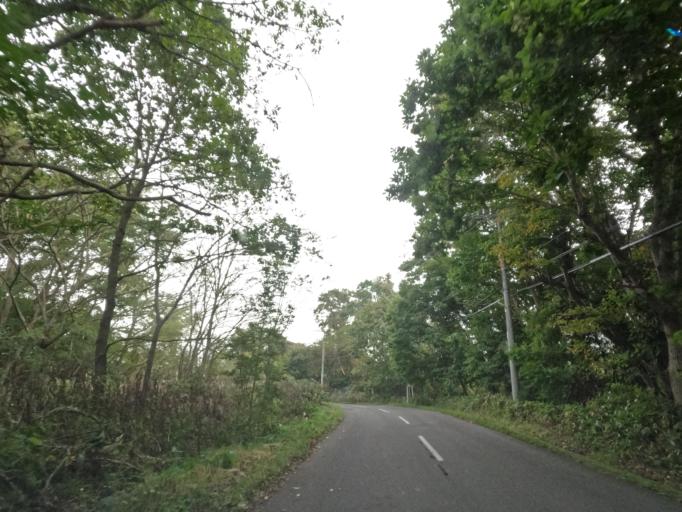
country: JP
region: Hokkaido
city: Date
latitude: 42.4109
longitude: 140.9157
